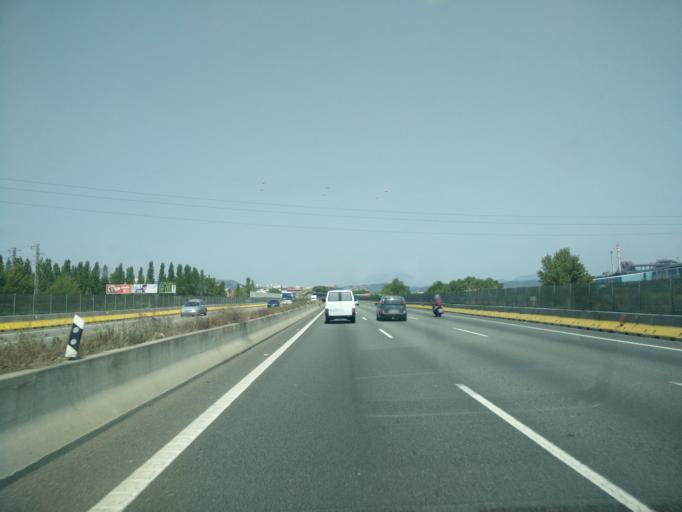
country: ES
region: Catalonia
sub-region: Provincia de Barcelona
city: Sant Andreu de la Barca
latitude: 41.4428
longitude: 1.9842
